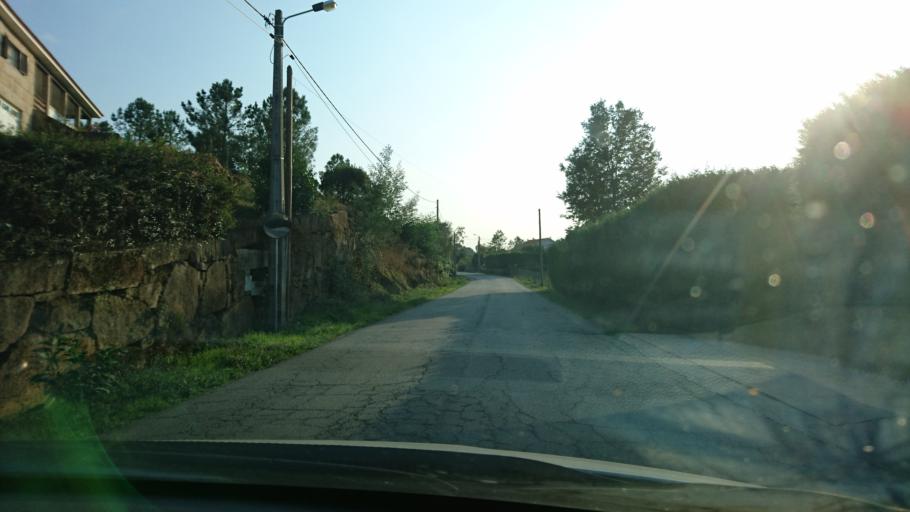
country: PT
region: Vila Real
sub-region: Mondim de Basto
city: Mondim de Basto
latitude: 41.4344
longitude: -7.9274
